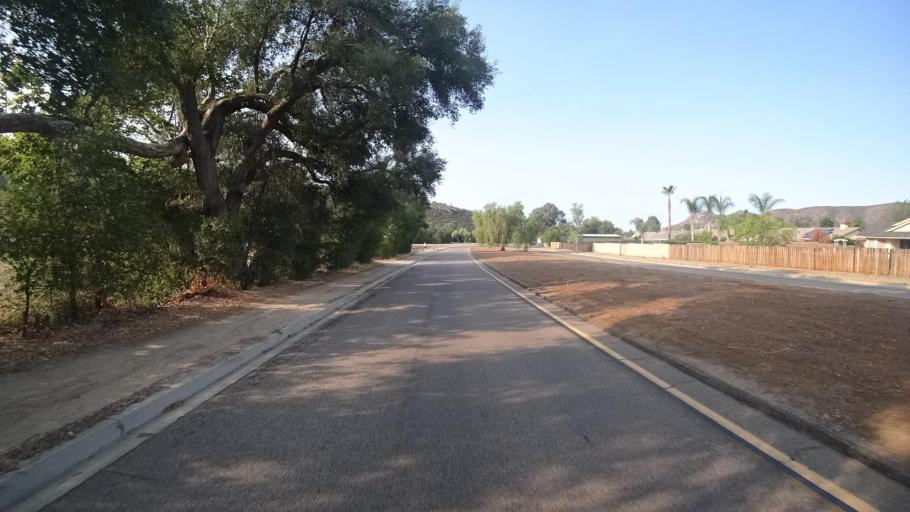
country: US
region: California
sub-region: San Diego County
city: San Diego Country Estates
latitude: 33.0127
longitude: -116.8075
